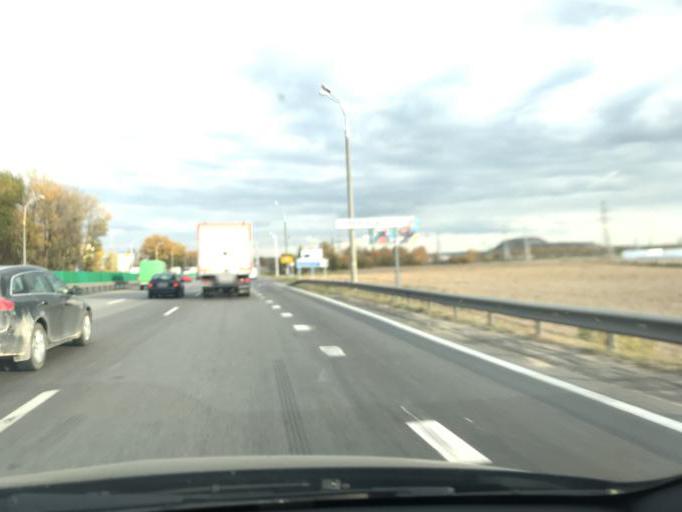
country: BY
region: Minsk
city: Syenitsa
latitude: 53.8329
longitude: 27.5681
